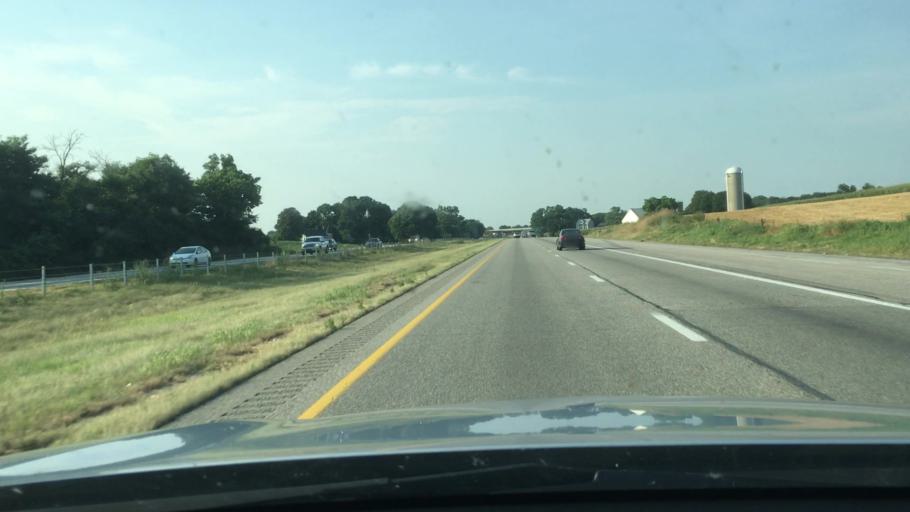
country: US
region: Pennsylvania
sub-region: Franklin County
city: Greencastle
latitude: 39.8224
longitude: -77.7007
